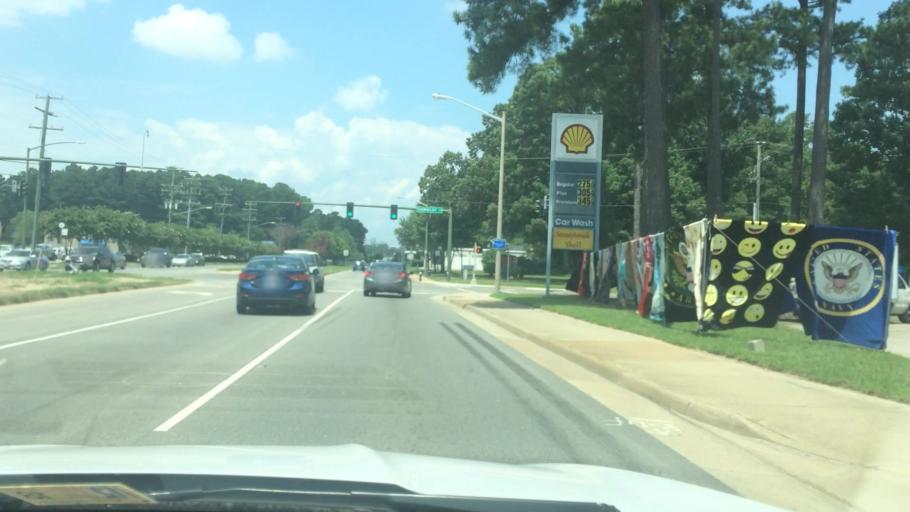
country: US
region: Virginia
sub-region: York County
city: Yorktown
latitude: 37.1507
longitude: -76.5533
